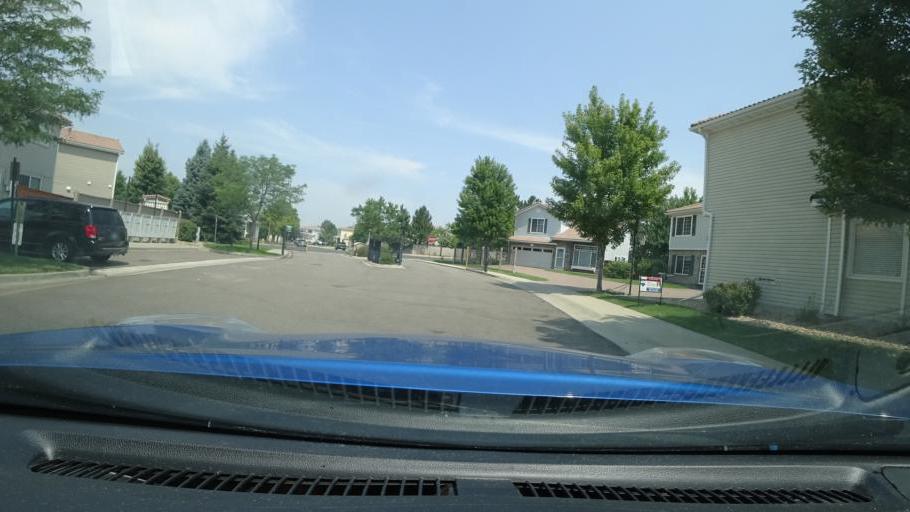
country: US
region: Colorado
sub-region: Adams County
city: Aurora
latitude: 39.7765
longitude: -104.7543
